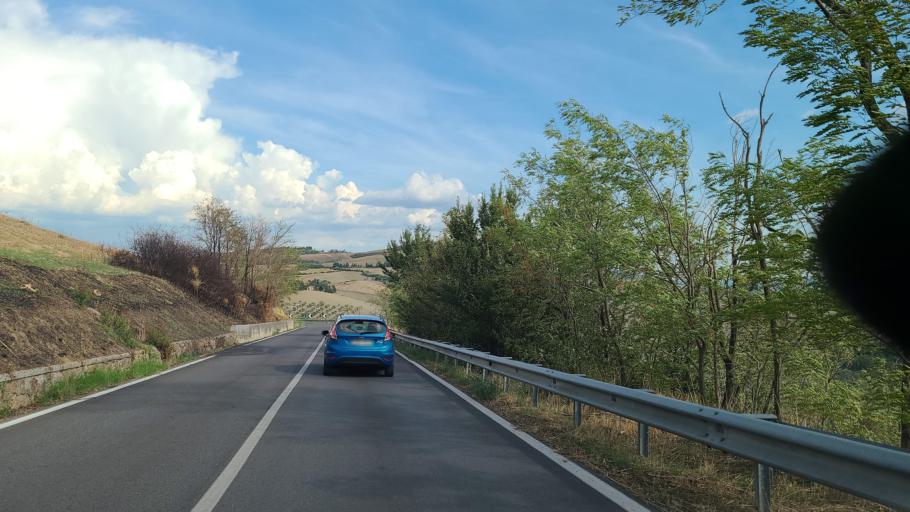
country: IT
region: Tuscany
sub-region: Province of Pisa
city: Volterra
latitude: 43.3935
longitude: 10.8895
